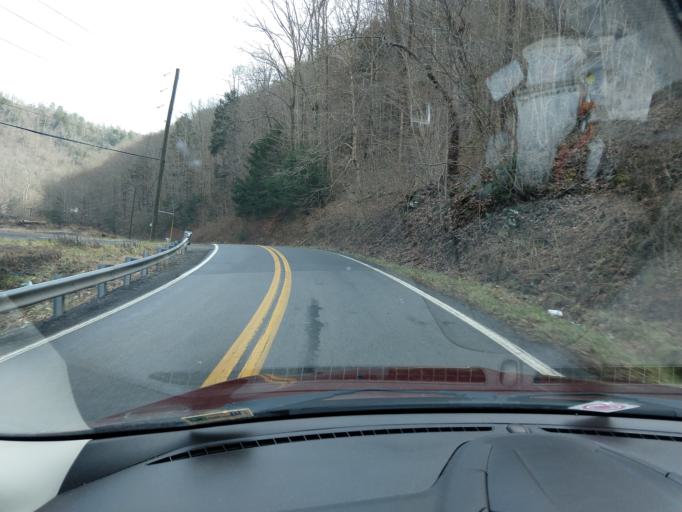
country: US
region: West Virginia
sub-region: McDowell County
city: Welch
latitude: 37.3439
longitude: -81.7554
